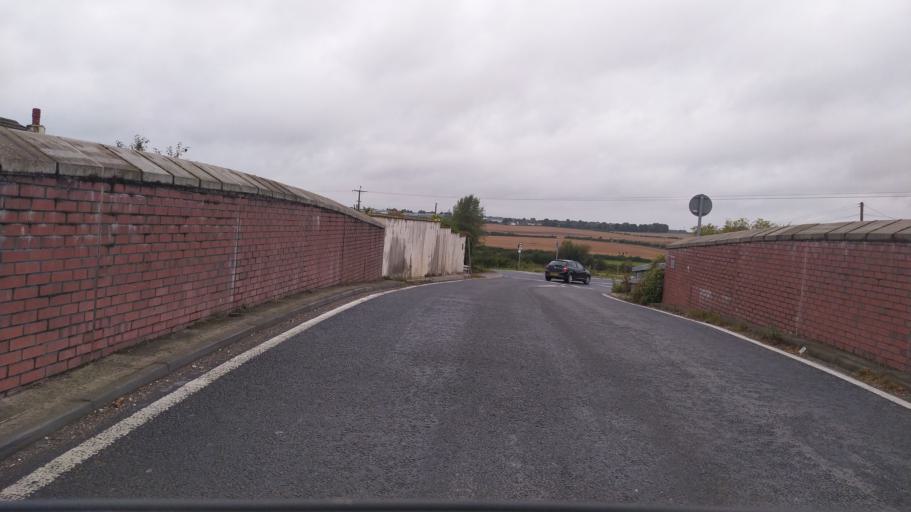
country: GB
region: England
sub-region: Wiltshire
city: Salisbury
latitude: 51.0957
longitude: -1.7601
